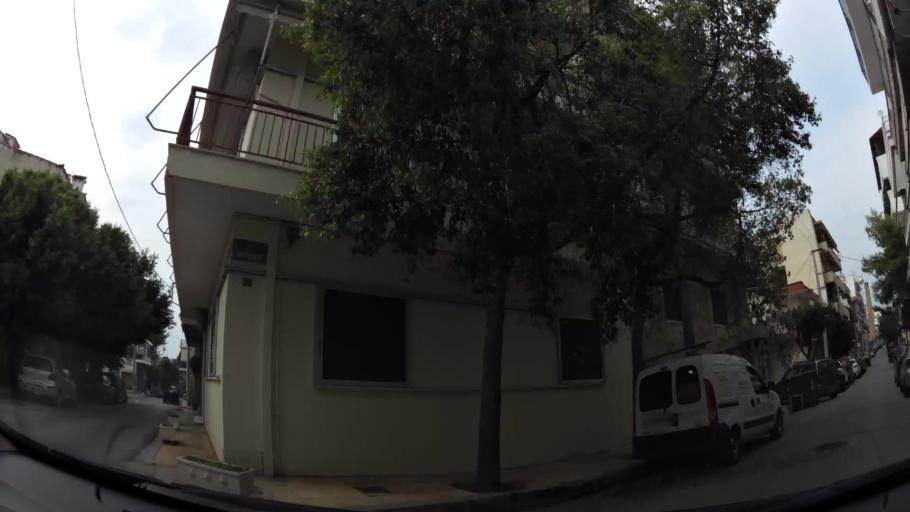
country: GR
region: Attica
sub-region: Nomarchia Athinas
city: Nea Ionia
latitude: 38.0476
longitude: 23.7520
